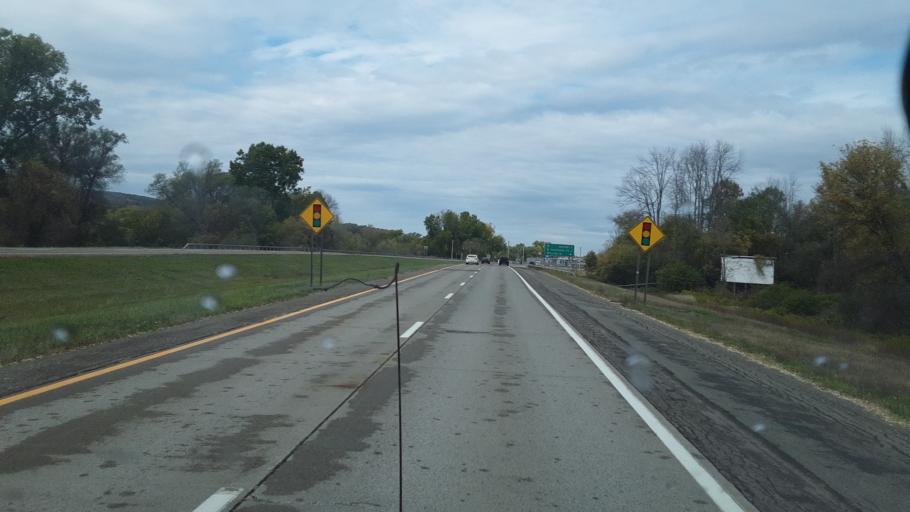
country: US
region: New York
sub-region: Steuben County
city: Hornell
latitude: 42.3604
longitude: -77.6706
